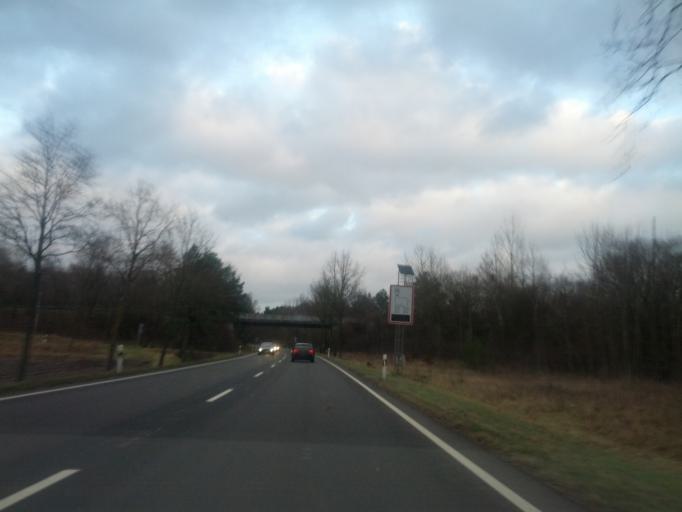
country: DE
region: Lower Saxony
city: Rotenburg
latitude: 53.1336
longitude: 9.4441
